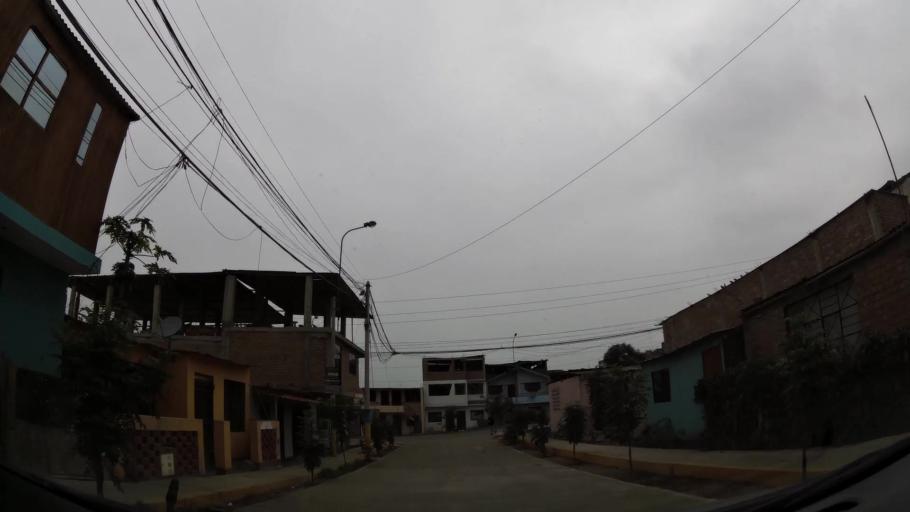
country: PE
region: Lima
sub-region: Lima
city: Surco
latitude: -12.2183
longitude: -76.9300
